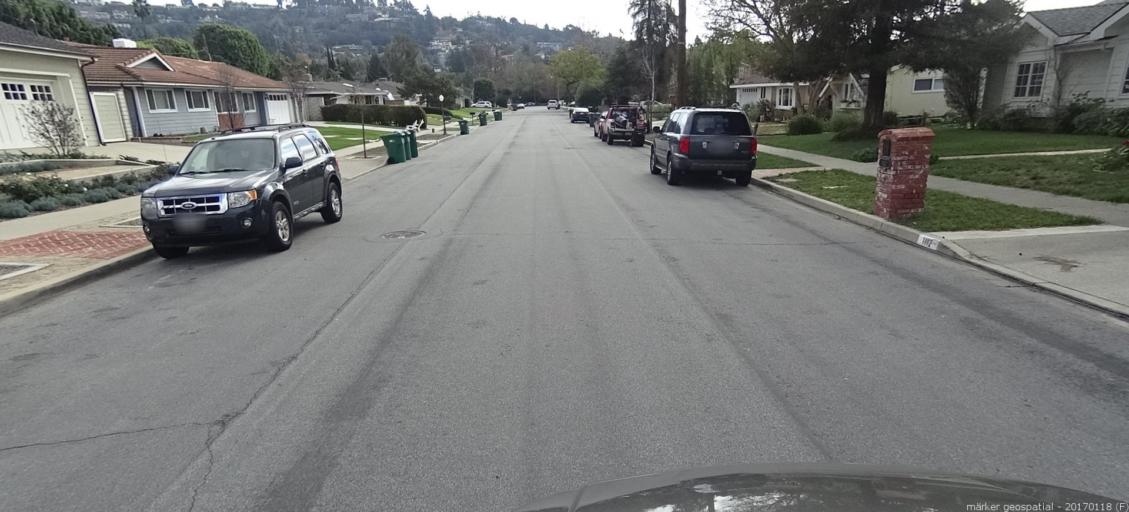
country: US
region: California
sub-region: Orange County
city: North Tustin
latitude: 33.7664
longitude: -117.7933
